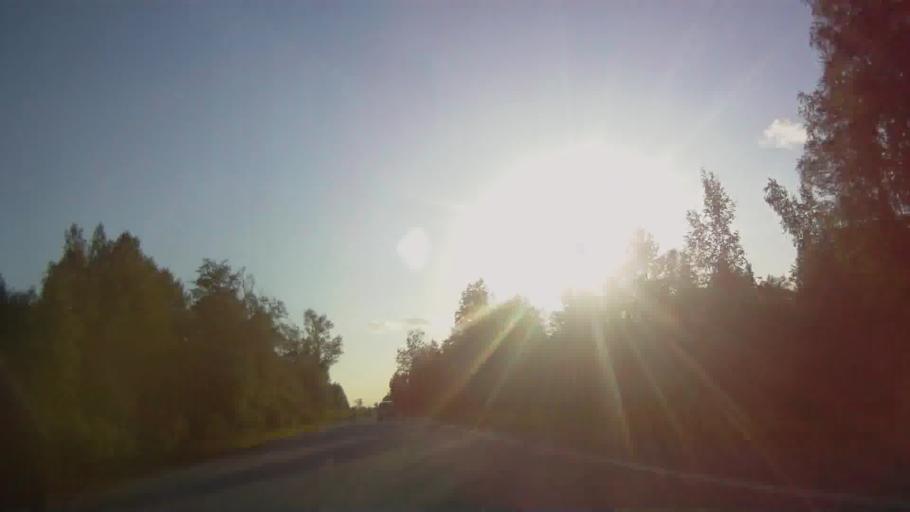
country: LV
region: Livani
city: Livani
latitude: 56.5308
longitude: 26.3543
